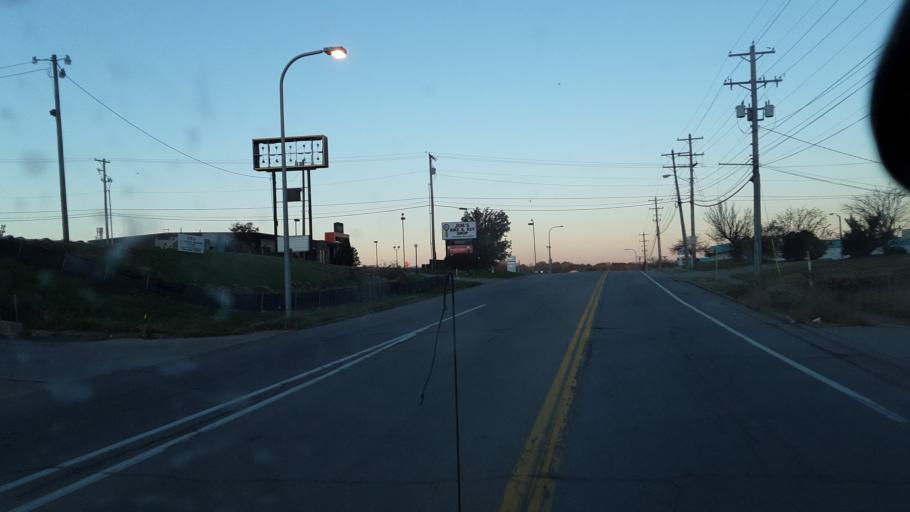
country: US
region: Missouri
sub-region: Boone County
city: Columbia
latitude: 38.9711
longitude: -92.3262
